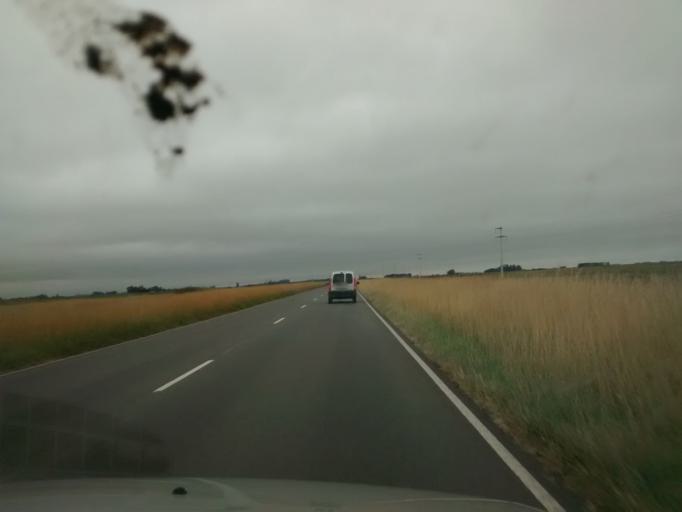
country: AR
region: Buenos Aires
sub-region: Partido de Ayacucho
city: Ayacucho
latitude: -37.0122
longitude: -58.5375
